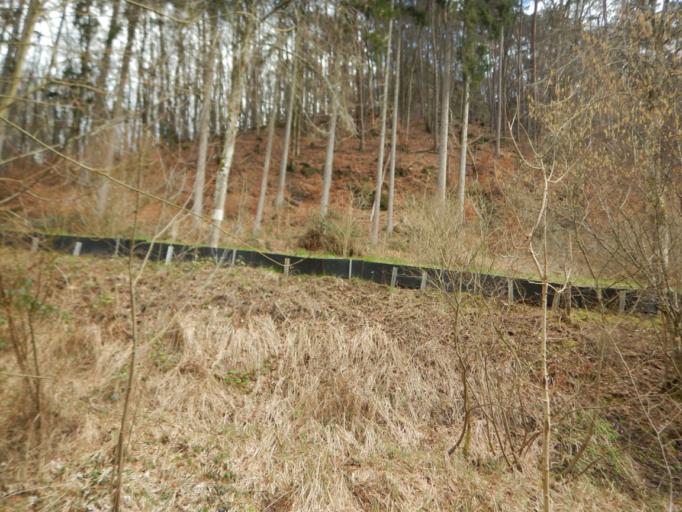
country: LU
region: Luxembourg
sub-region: Canton de Mersch
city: Tuntange
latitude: 49.7208
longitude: 6.0599
